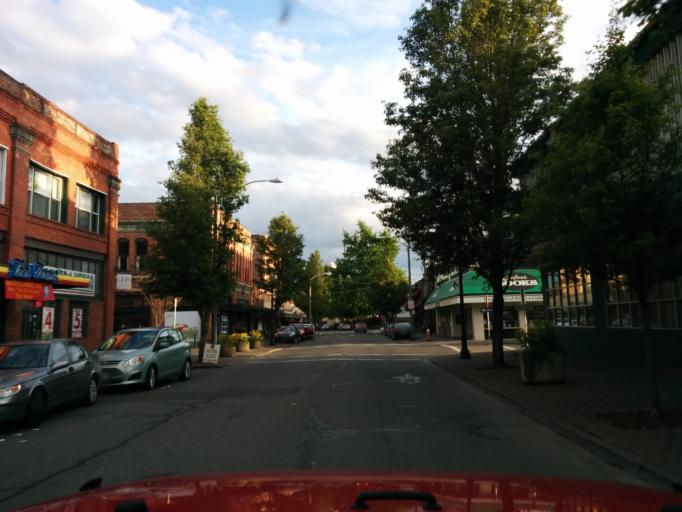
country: US
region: Washington
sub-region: Skagit County
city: Mount Vernon
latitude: 48.4185
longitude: -122.3384
